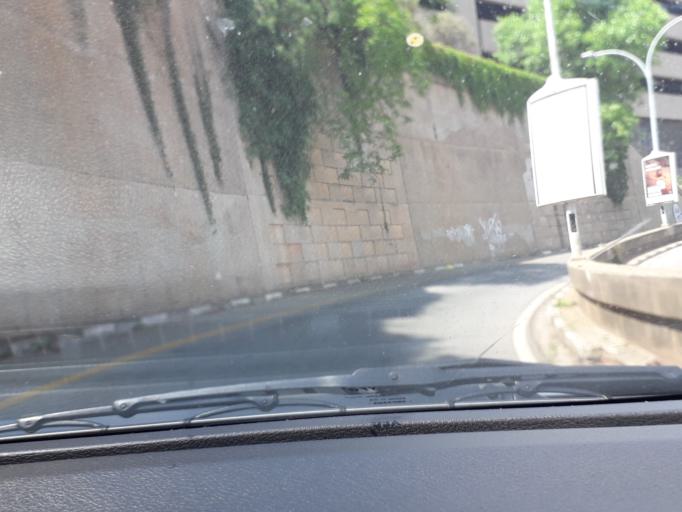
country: ZA
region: Gauteng
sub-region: City of Johannesburg Metropolitan Municipality
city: Johannesburg
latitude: -26.1839
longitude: 28.0333
